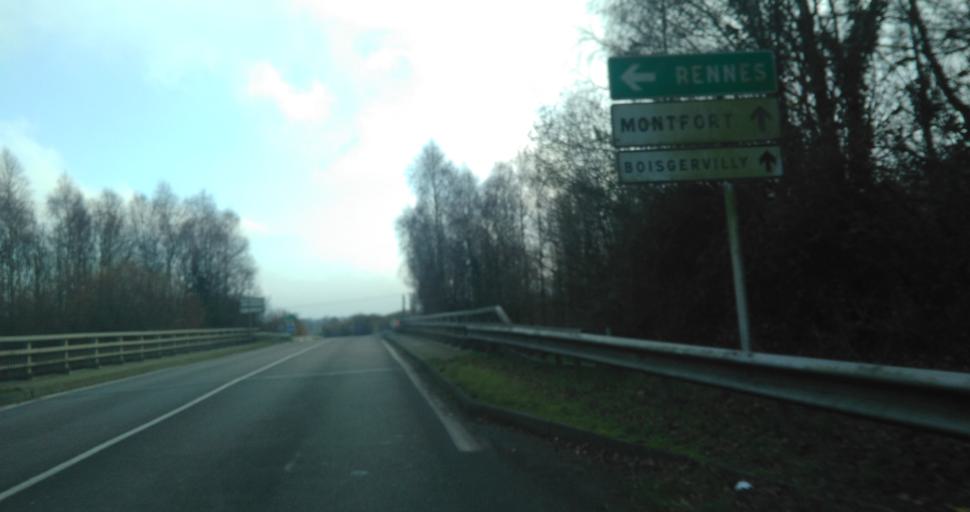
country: FR
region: Brittany
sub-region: Departement d'Ille-et-Vilaine
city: Saint-Meen-le-Grand
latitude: 48.1882
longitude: -2.1696
